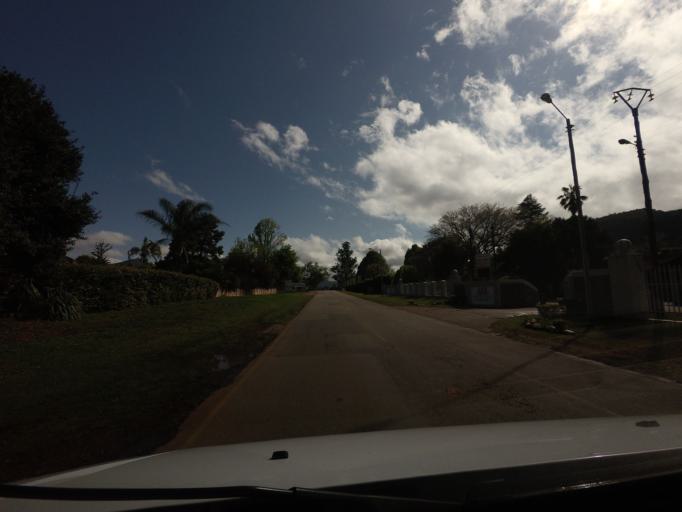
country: ZA
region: Mpumalanga
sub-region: Ehlanzeni District
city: Graksop
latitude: -25.0924
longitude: 30.7738
